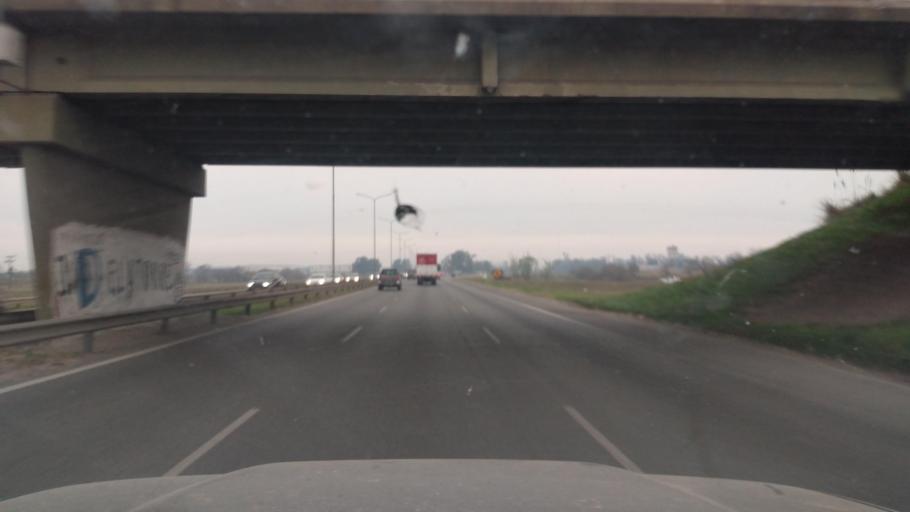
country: AR
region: Buenos Aires
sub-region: Partido de General San Martin
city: General San Martin
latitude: -34.5170
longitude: -58.5908
